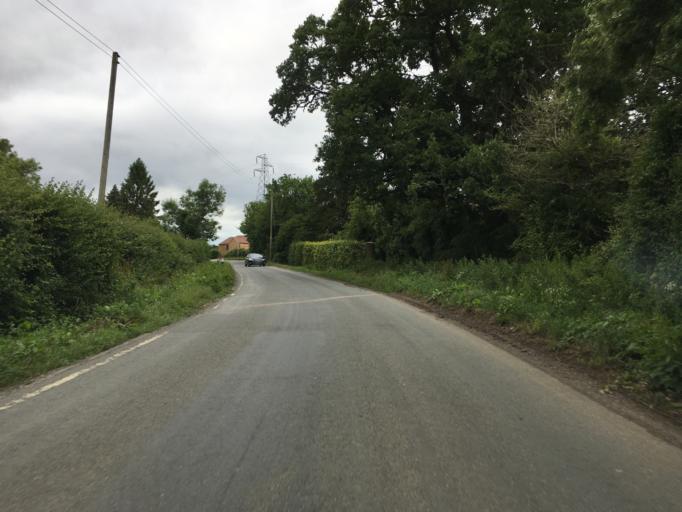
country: GB
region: England
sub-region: Gloucestershire
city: Cinderford
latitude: 51.7854
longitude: -2.3959
